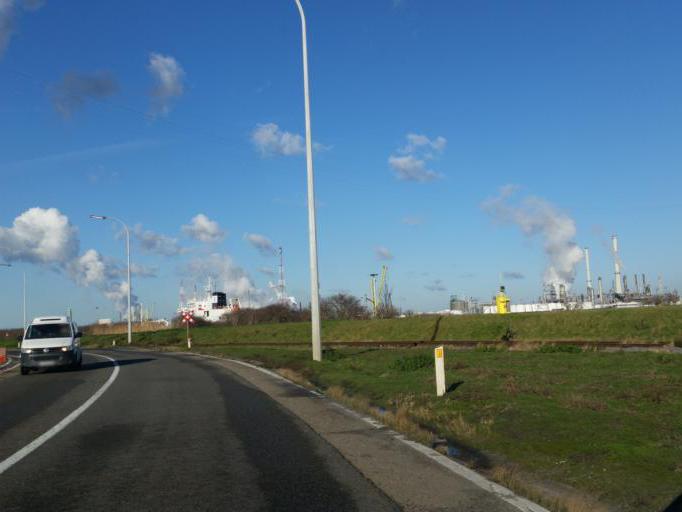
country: BE
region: Flanders
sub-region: Provincie Antwerpen
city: Zwijndrecht
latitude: 51.2422
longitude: 4.3380
